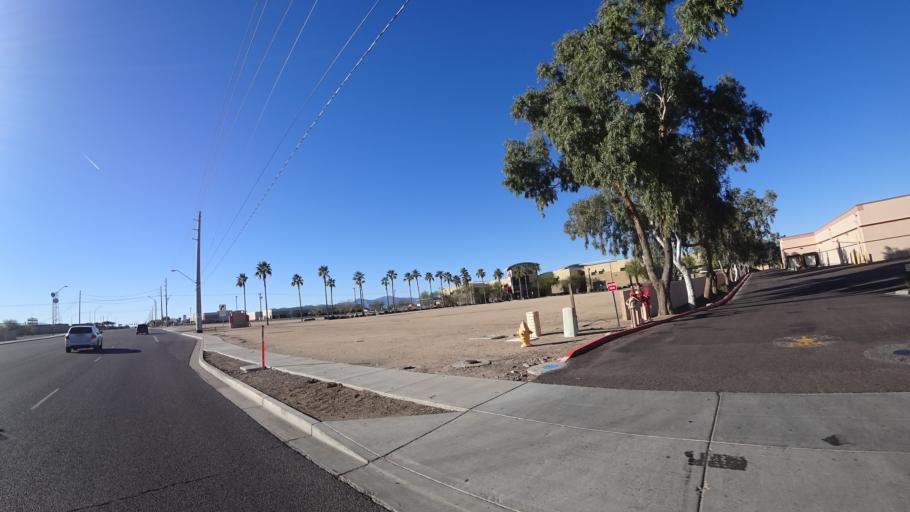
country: US
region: Arizona
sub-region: Maricopa County
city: Goodyear
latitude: 33.4499
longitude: -112.3603
